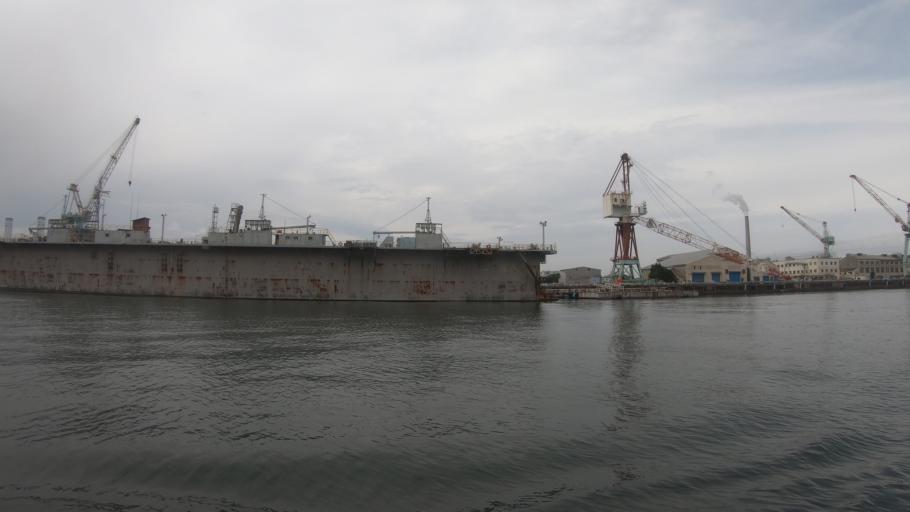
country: JP
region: Kanagawa
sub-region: Kawasaki-shi
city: Kawasaki
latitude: 35.4893
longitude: 139.6920
